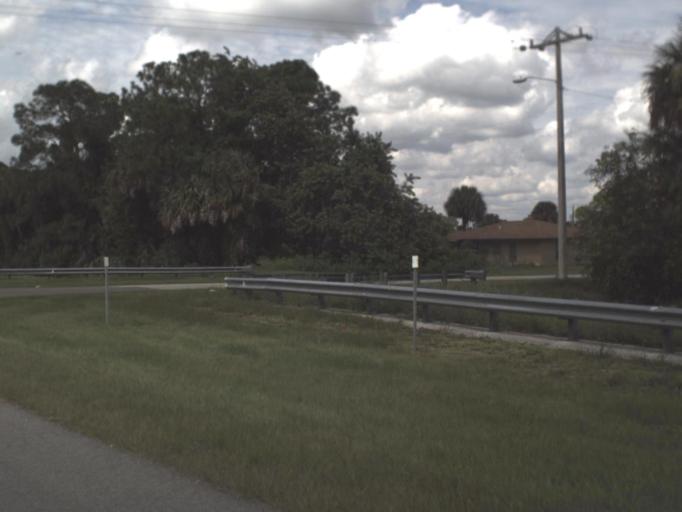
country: US
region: Florida
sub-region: Collier County
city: Immokalee
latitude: 26.4009
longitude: -81.3890
